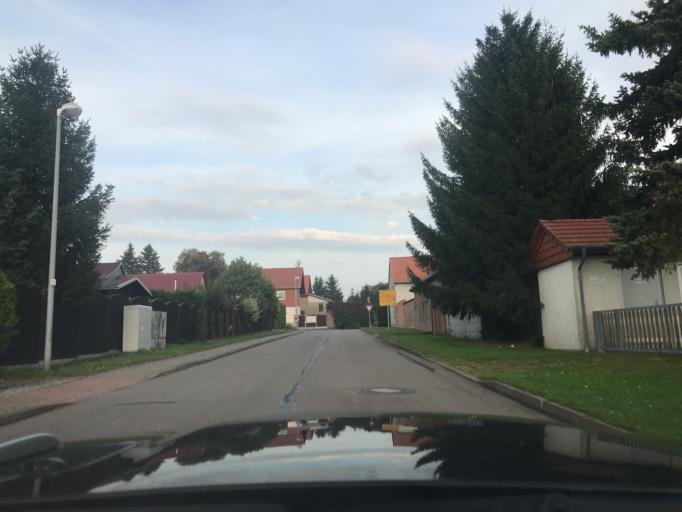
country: DE
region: Thuringia
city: Sollstedt
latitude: 51.2718
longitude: 10.4813
